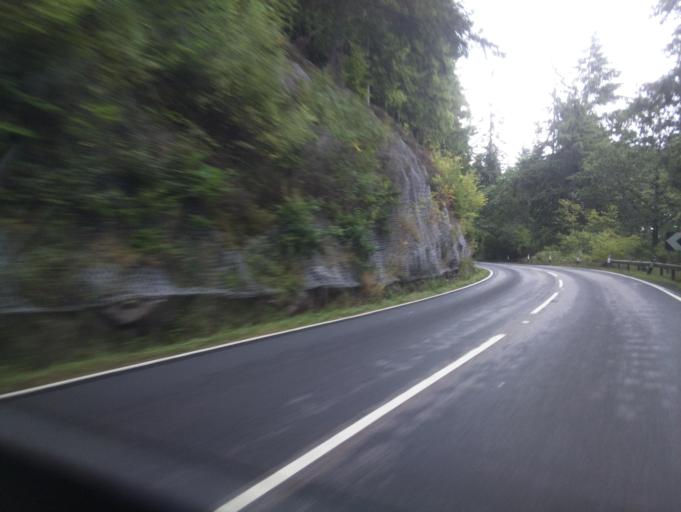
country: GB
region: Scotland
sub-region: Highland
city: Beauly
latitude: 57.2769
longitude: -4.4971
